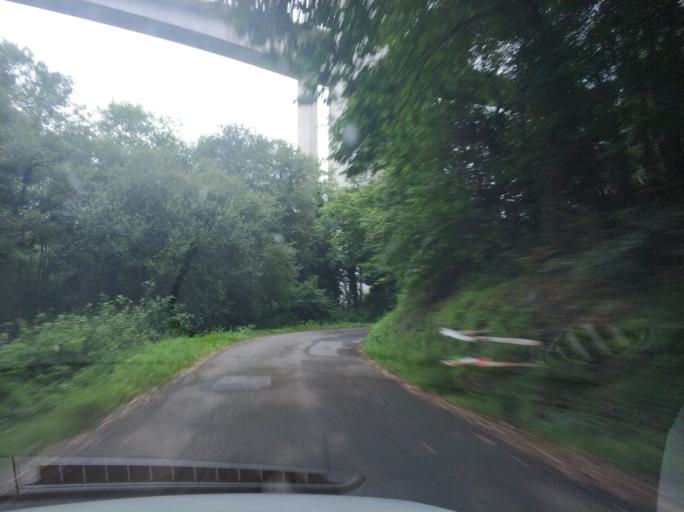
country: ES
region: Asturias
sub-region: Province of Asturias
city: Cudillero
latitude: 43.5547
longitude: -6.1904
